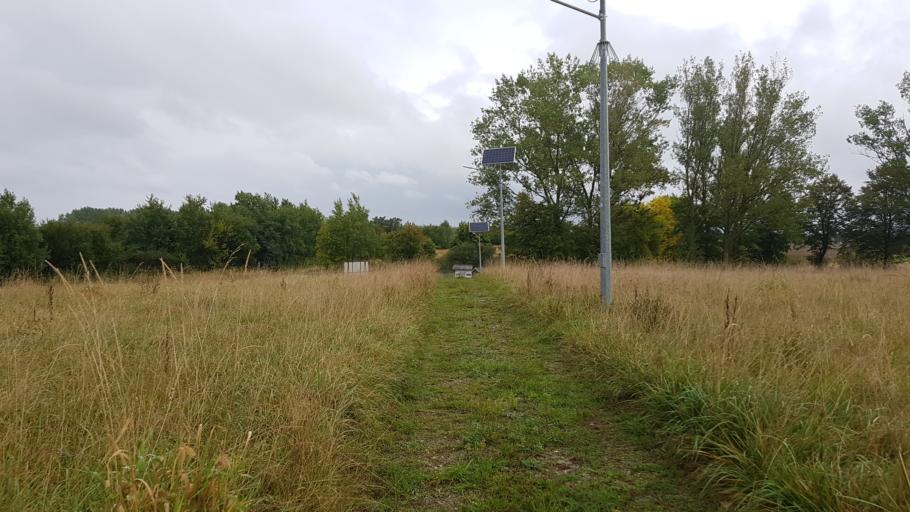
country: PL
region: West Pomeranian Voivodeship
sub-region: Powiat gryficki
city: Trzebiatow
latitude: 54.0730
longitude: 15.2107
